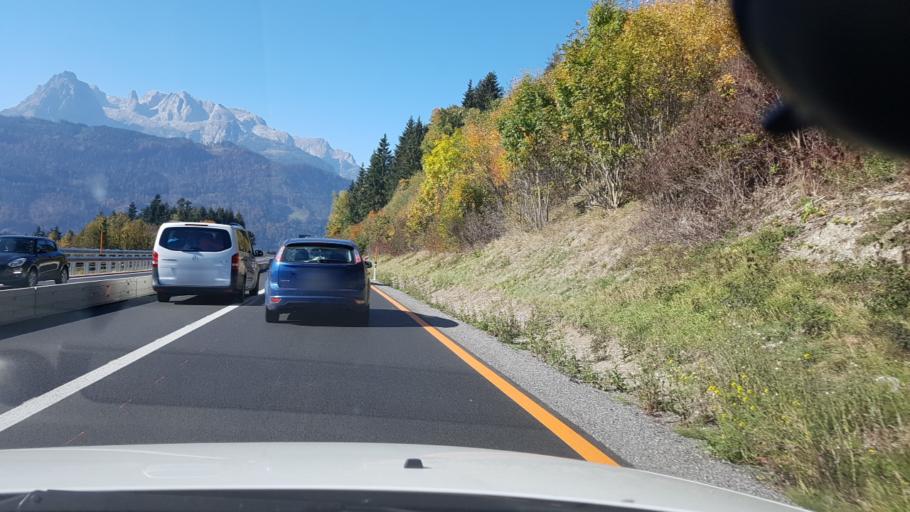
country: AT
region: Salzburg
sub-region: Politischer Bezirk Sankt Johann im Pongau
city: Werfenweng
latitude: 47.4354
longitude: 13.2498
